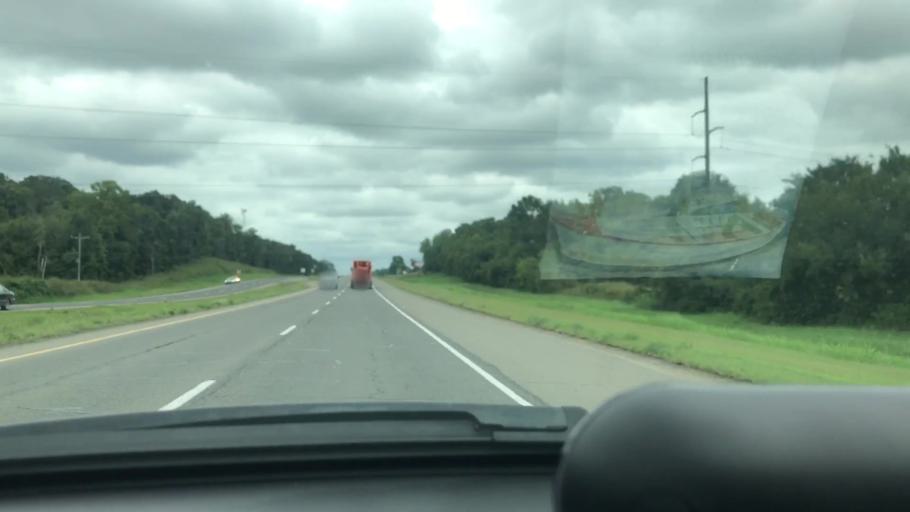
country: US
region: Oklahoma
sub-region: Muskogee County
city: Muskogee
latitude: 35.8200
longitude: -95.4026
